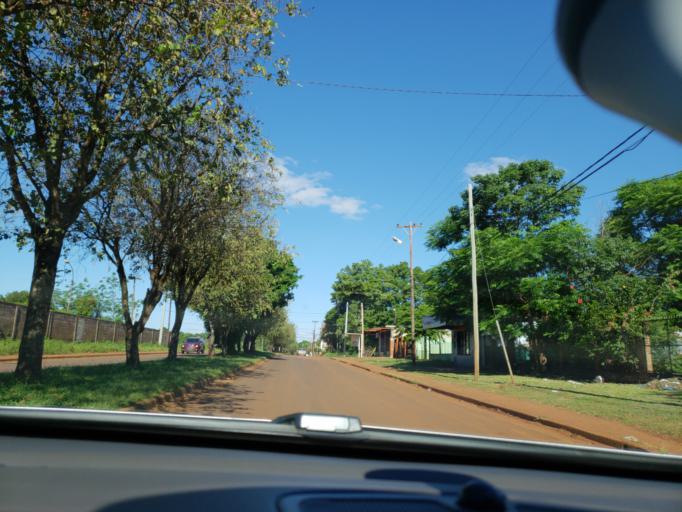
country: AR
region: Misiones
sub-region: Departamento de Capital
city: Posadas
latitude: -27.3826
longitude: -55.9461
